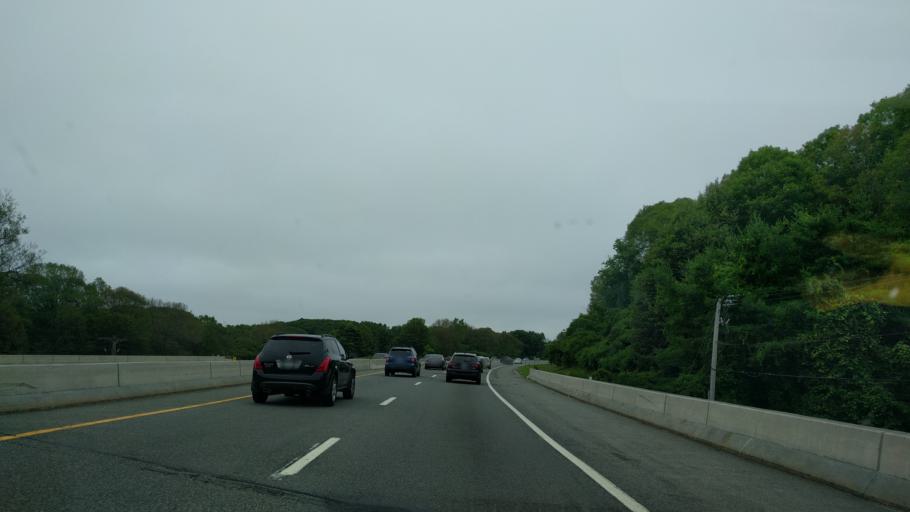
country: US
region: Rhode Island
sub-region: Washington County
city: Exeter
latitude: 41.5949
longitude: -71.4989
